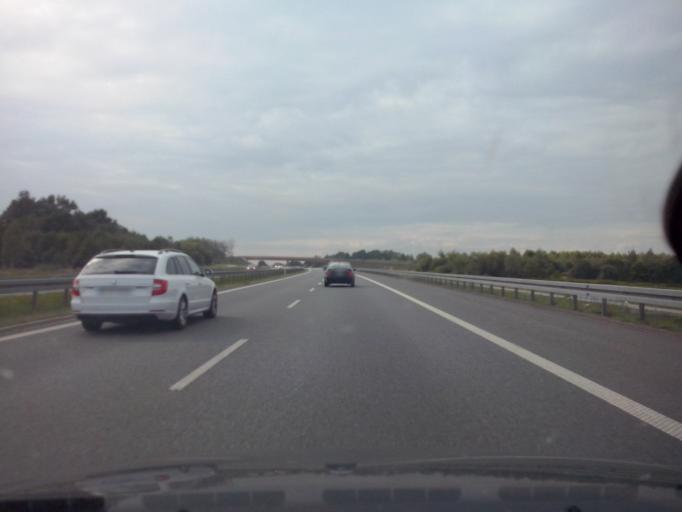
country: PL
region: Lesser Poland Voivodeship
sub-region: Powiat bochenski
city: Borek
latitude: 50.0092
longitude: 20.5249
